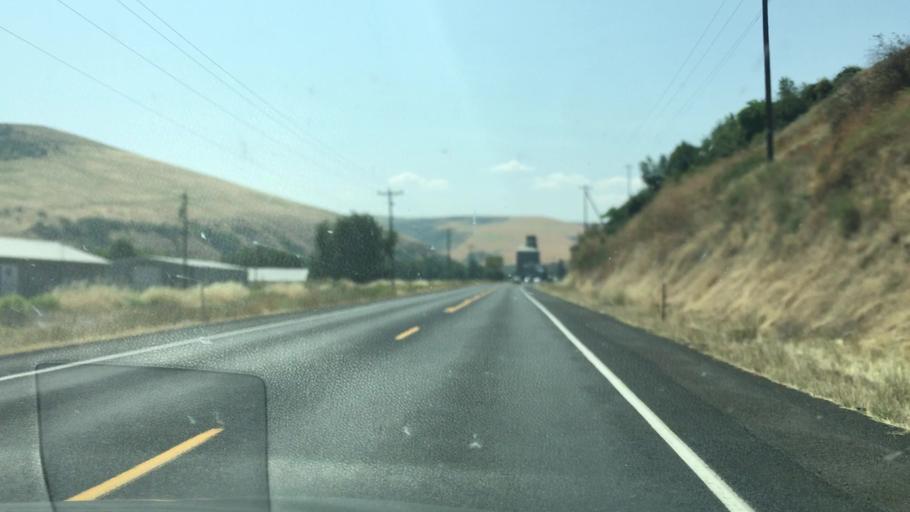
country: US
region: Idaho
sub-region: Nez Perce County
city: Lapwai
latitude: 46.3795
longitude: -116.7960
